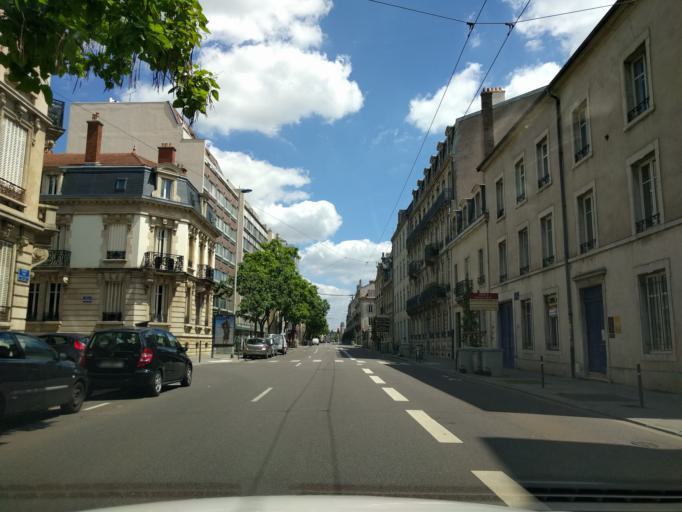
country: FR
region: Lorraine
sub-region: Departement de Meurthe-et-Moselle
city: Nancy
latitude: 48.6871
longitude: 6.1694
